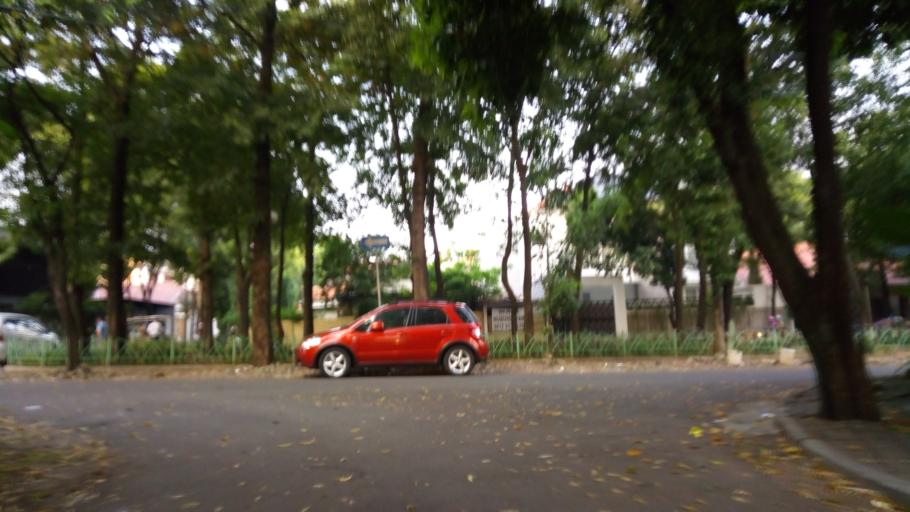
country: ID
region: Jakarta Raya
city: Jakarta
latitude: -6.2440
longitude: 106.7894
